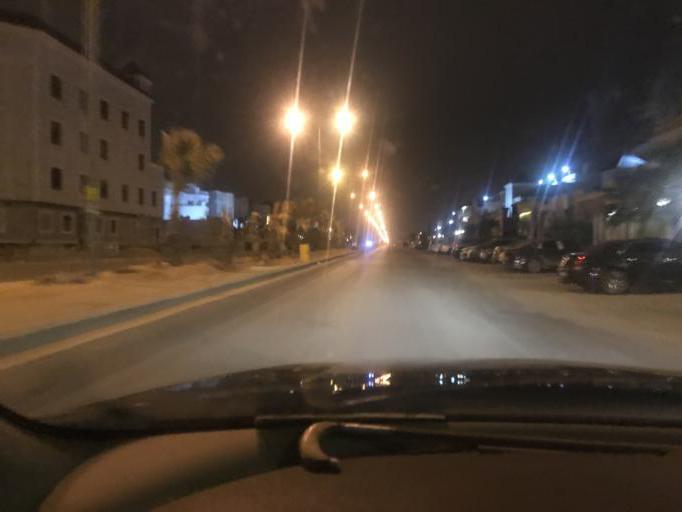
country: SA
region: Ar Riyad
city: Riyadh
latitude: 24.8063
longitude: 46.6817
